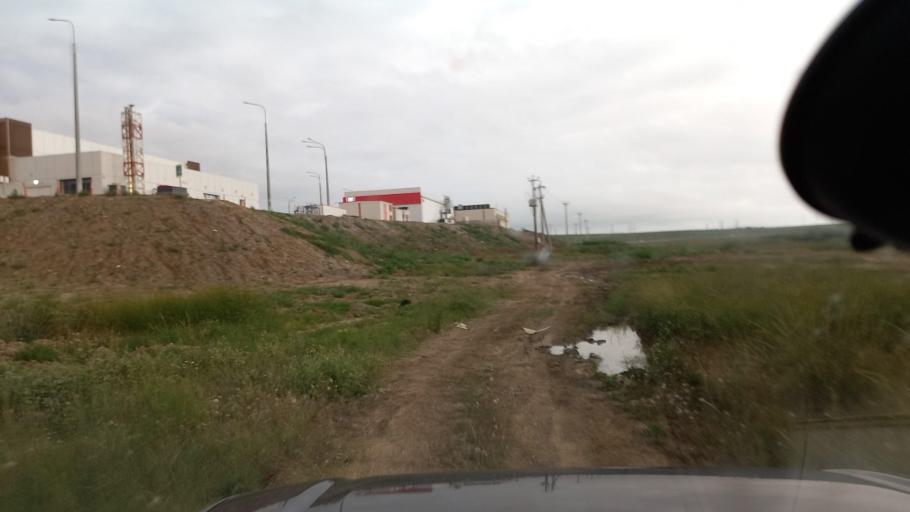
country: RU
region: Krasnodarskiy
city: Taman'
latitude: 45.2114
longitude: 36.7584
